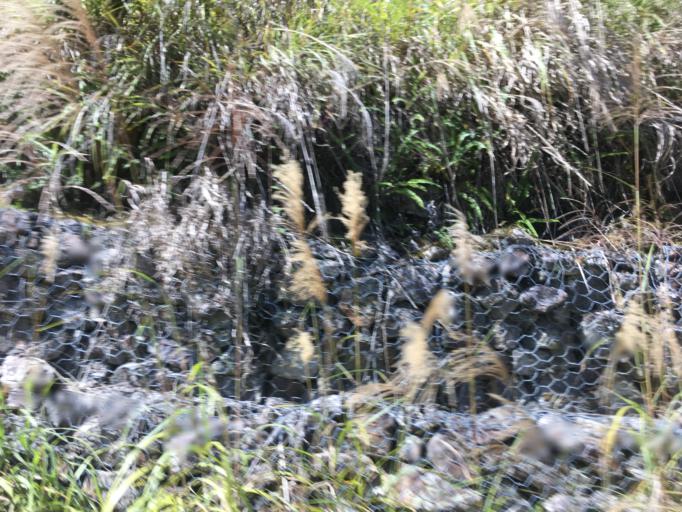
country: TW
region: Taiwan
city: Daxi
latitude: 24.5738
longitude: 121.4144
